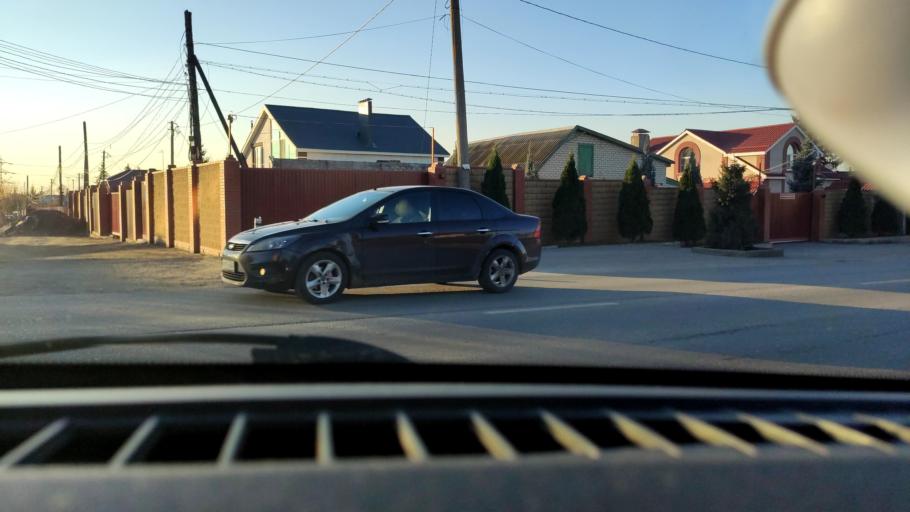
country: RU
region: Samara
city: Samara
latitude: 53.1769
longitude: 50.1832
